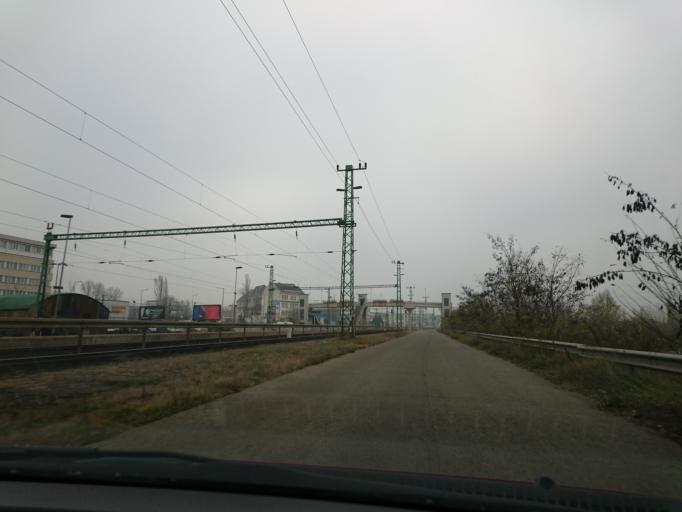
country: HU
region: Budapest
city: Budapest XX. keruelet
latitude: 47.4568
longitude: 19.0841
